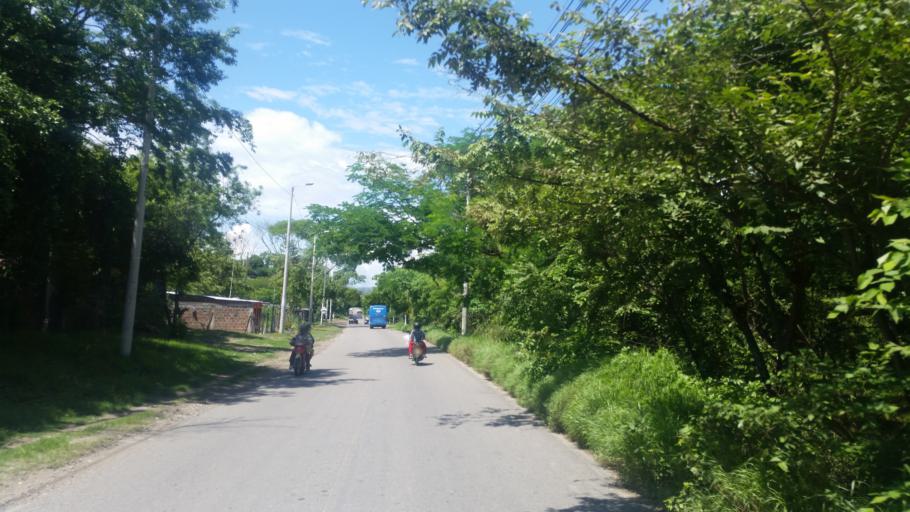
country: CO
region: Huila
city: Neiva
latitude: 2.9848
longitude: -75.2787
